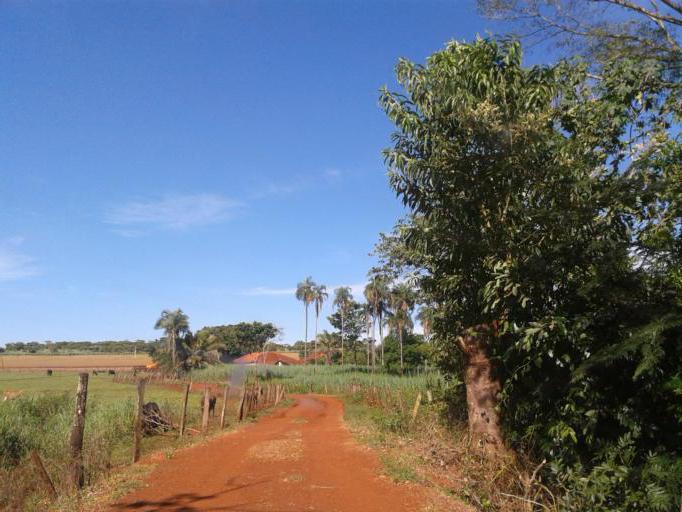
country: BR
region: Minas Gerais
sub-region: Capinopolis
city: Capinopolis
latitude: -18.6750
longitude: -49.6366
